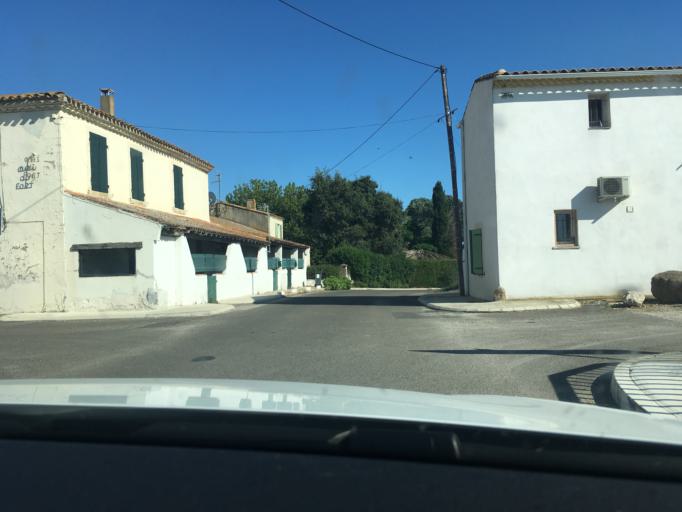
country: FR
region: Provence-Alpes-Cote d'Azur
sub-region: Departement des Bouches-du-Rhone
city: Saintes-Maries-de-la-Mer
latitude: 43.5446
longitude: 4.3471
